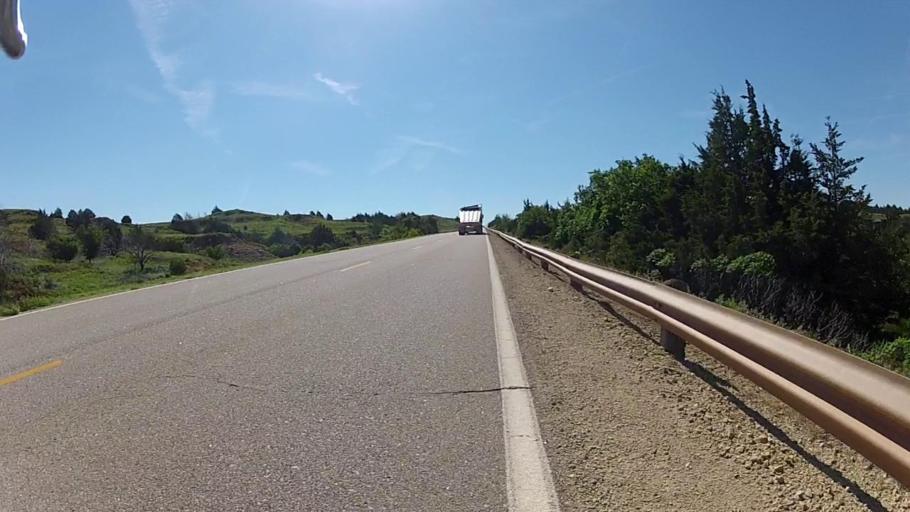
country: US
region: Kansas
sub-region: Barber County
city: Medicine Lodge
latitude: 37.2808
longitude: -98.7475
